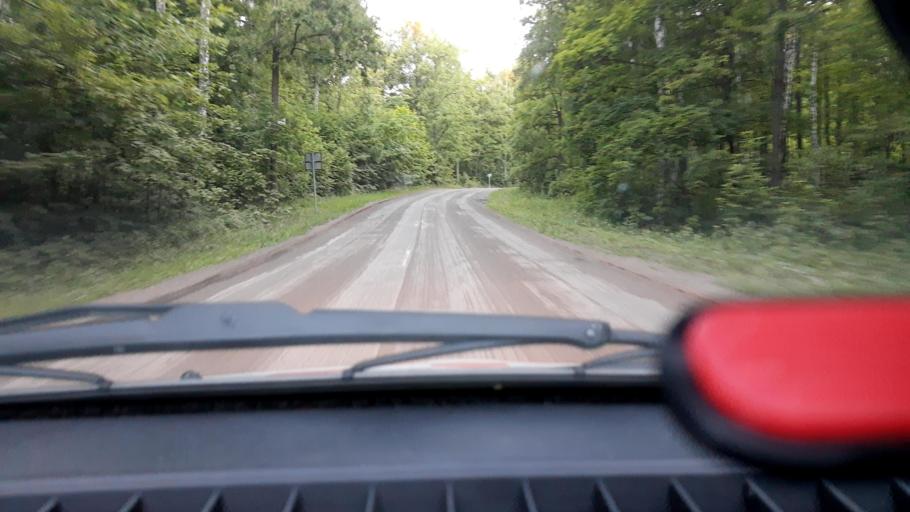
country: RU
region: Bashkortostan
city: Avdon
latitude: 54.6480
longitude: 55.7013
